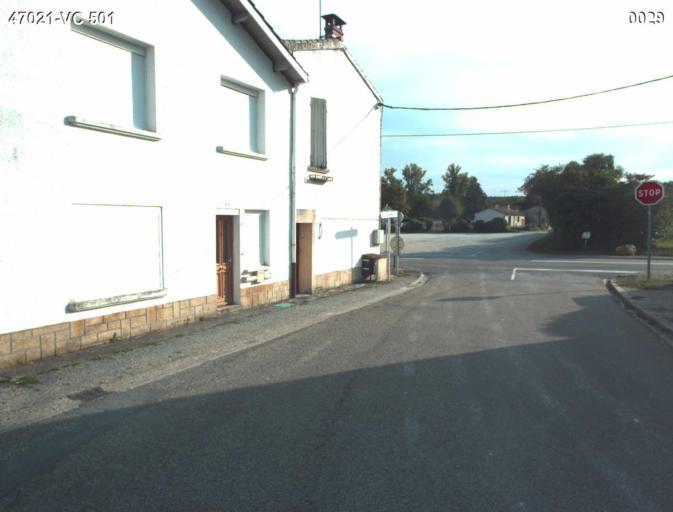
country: FR
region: Aquitaine
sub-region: Departement du Lot-et-Garonne
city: Barbaste
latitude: 44.1781
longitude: 0.2553
